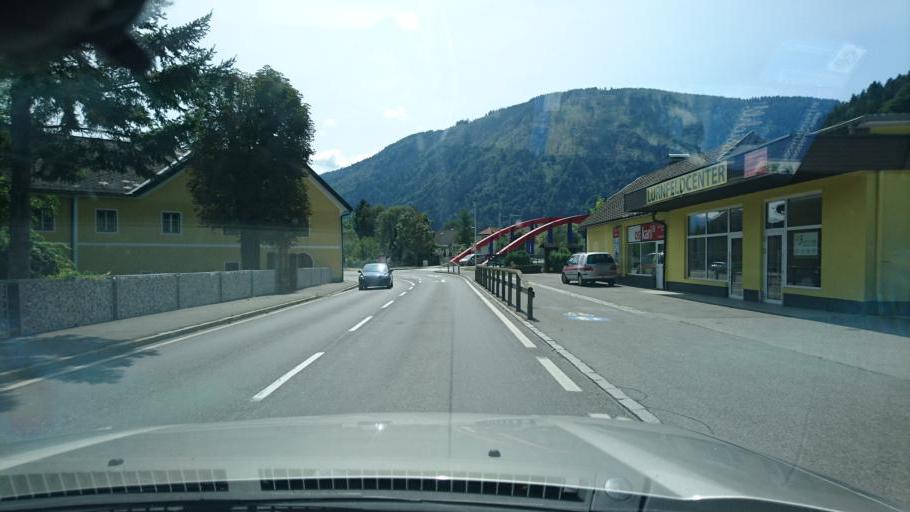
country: AT
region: Carinthia
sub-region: Politischer Bezirk Spittal an der Drau
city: Sachsenburg
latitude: 46.8384
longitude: 13.3693
